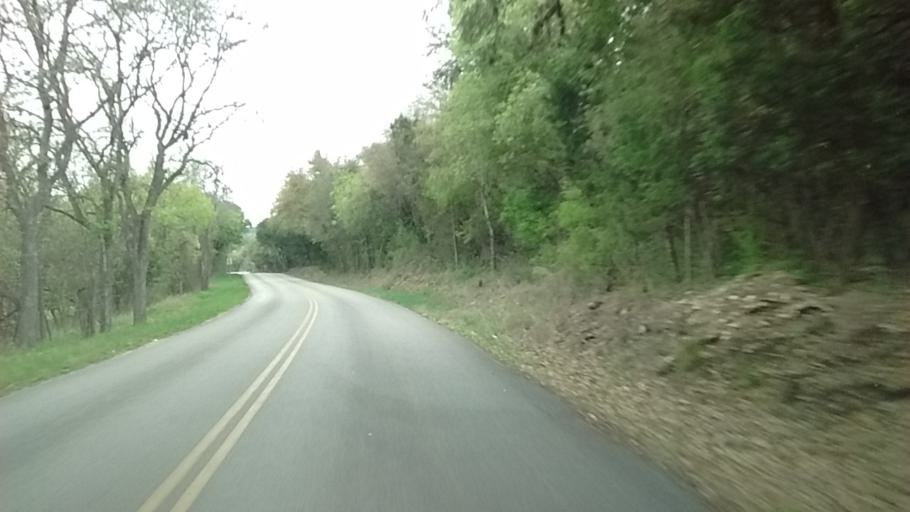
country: US
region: Texas
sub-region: Comal County
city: Canyon Lake
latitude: 29.8111
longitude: -98.1740
